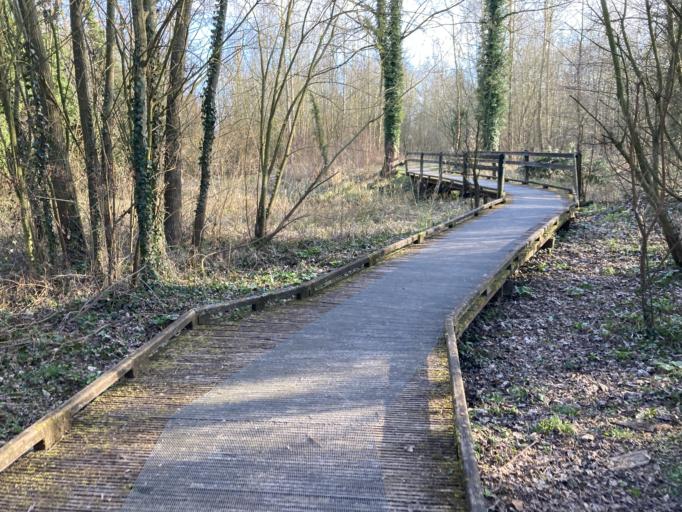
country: FR
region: Nord-Pas-de-Calais
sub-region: Departement du Pas-de-Calais
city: Annequin
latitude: 50.5213
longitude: 2.7101
